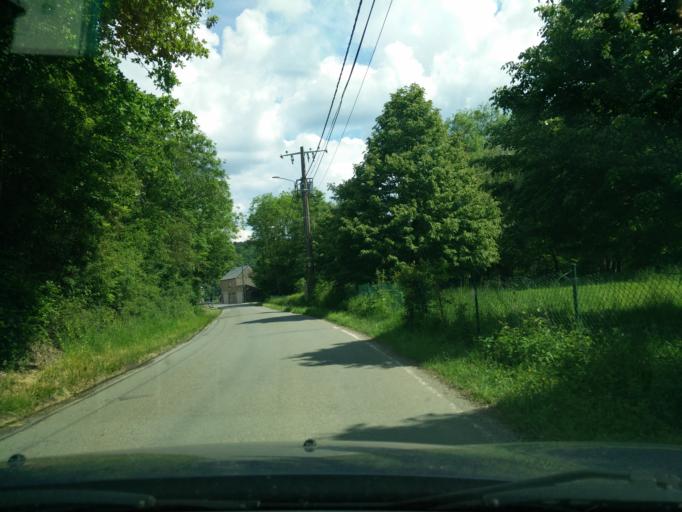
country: BE
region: Wallonia
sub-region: Province de Namur
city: Couvin
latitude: 50.0848
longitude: 4.5658
